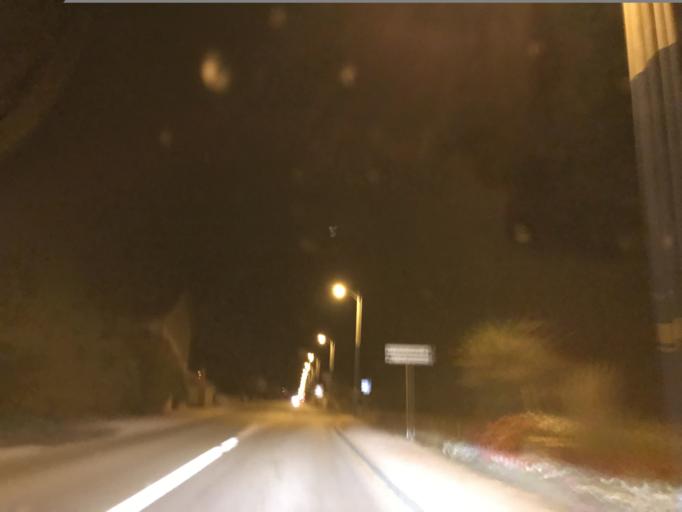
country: FR
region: Auvergne
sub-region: Departement du Puy-de-Dome
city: Puy-Guillaume
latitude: 45.9694
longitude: 3.4794
